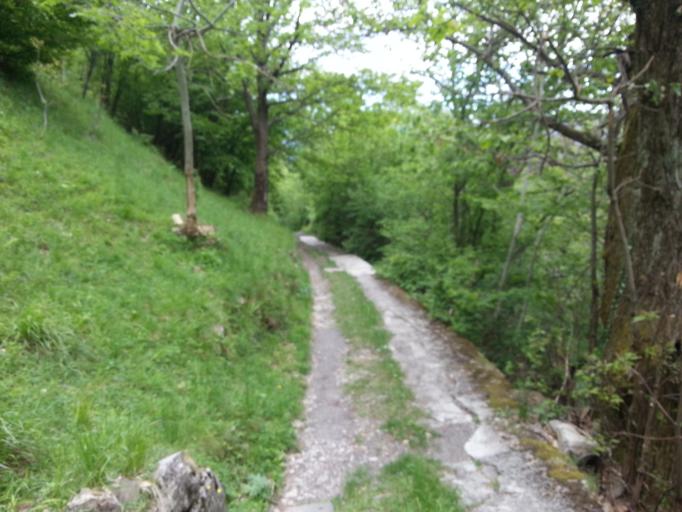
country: IT
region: Lombardy
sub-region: Provincia di Como
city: Ossuccio
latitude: 45.9915
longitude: 9.1777
